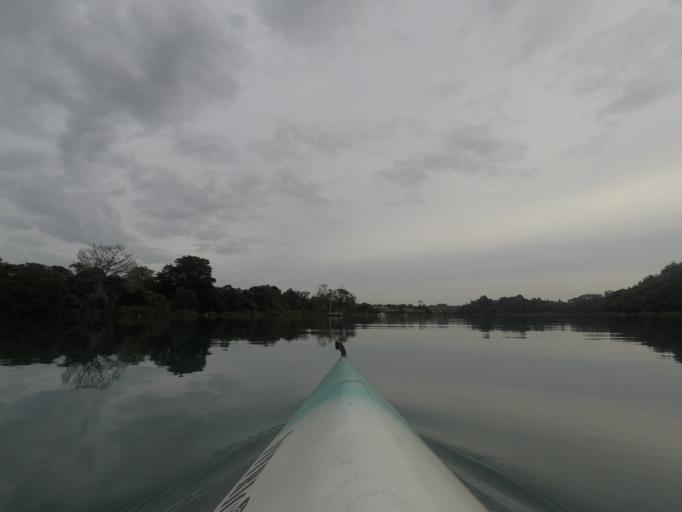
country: NZ
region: Auckland
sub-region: Auckland
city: Rothesay Bay
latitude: -36.6727
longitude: 174.7184
